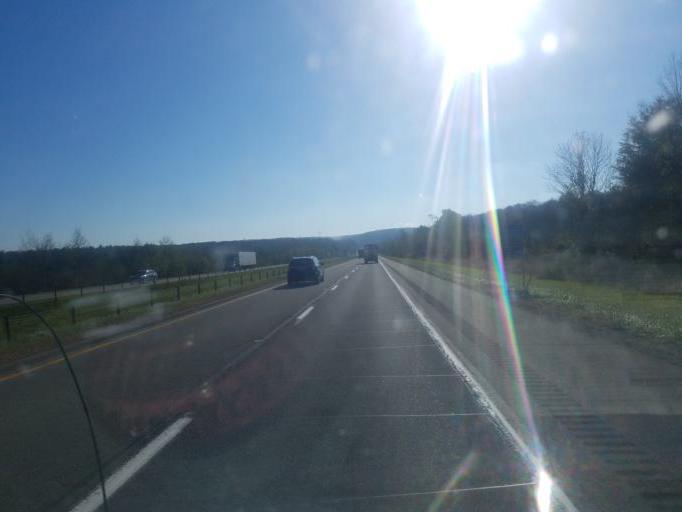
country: US
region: Pennsylvania
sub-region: Cambria County
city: Cresson
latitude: 40.4567
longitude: -78.6211
